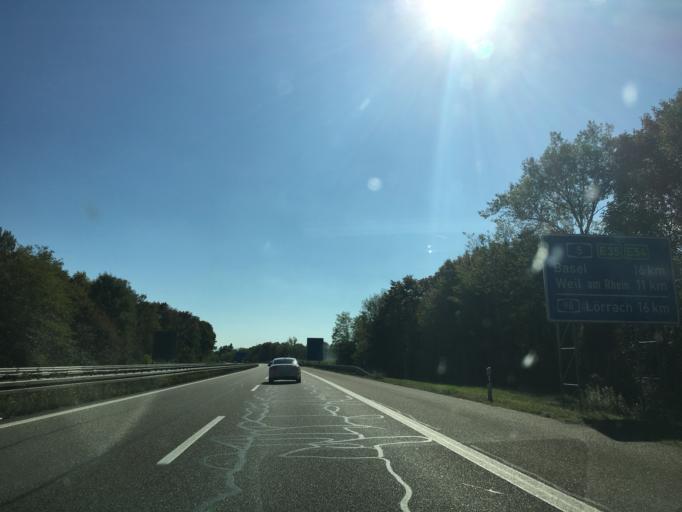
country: FR
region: Alsace
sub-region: Departement du Haut-Rhin
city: Kembs
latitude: 47.6725
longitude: 7.5236
